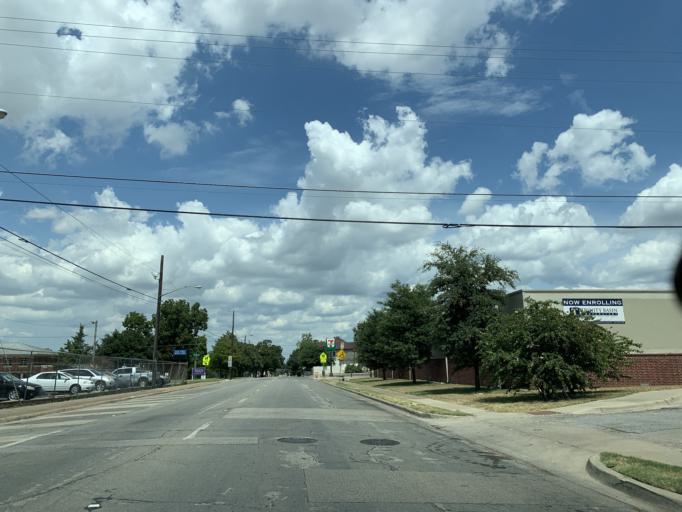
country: US
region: Texas
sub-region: Dallas County
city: Dallas
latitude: 32.7456
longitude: -96.8376
